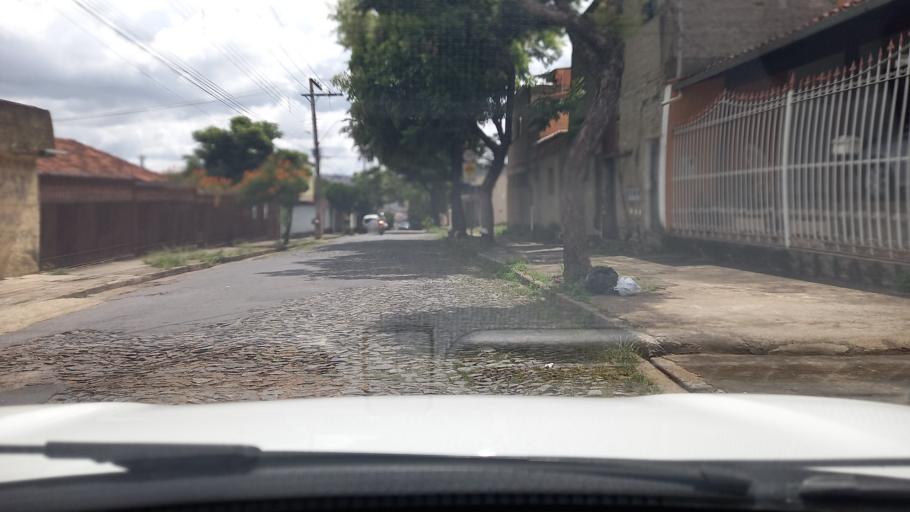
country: BR
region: Minas Gerais
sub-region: Contagem
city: Contagem
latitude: -19.9017
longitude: -44.0136
